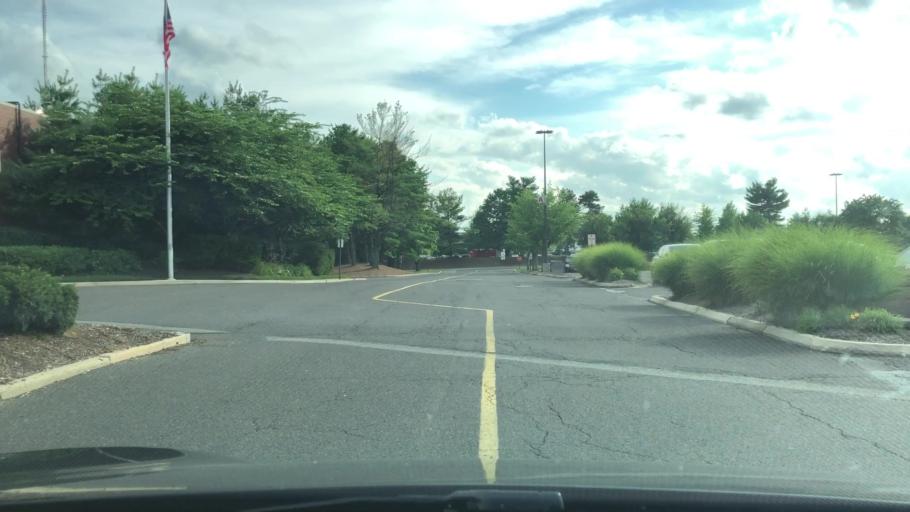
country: US
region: New Jersey
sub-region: Mercer County
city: Lawrenceville
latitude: 40.2902
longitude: -74.6836
